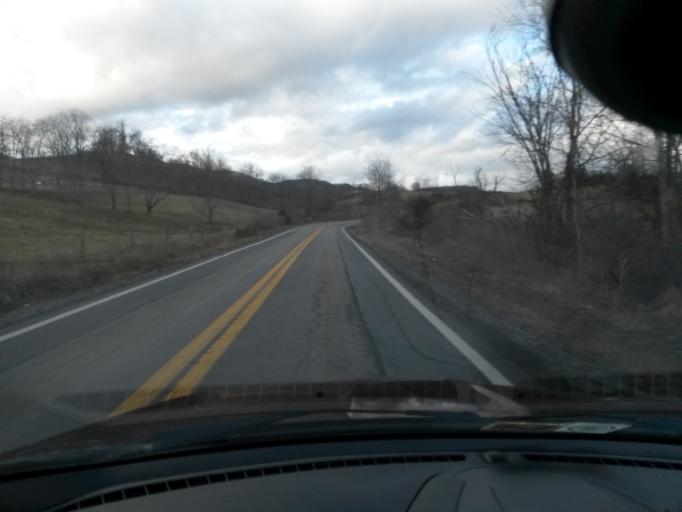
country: US
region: West Virginia
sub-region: Monroe County
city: Union
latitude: 37.5830
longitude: -80.5496
